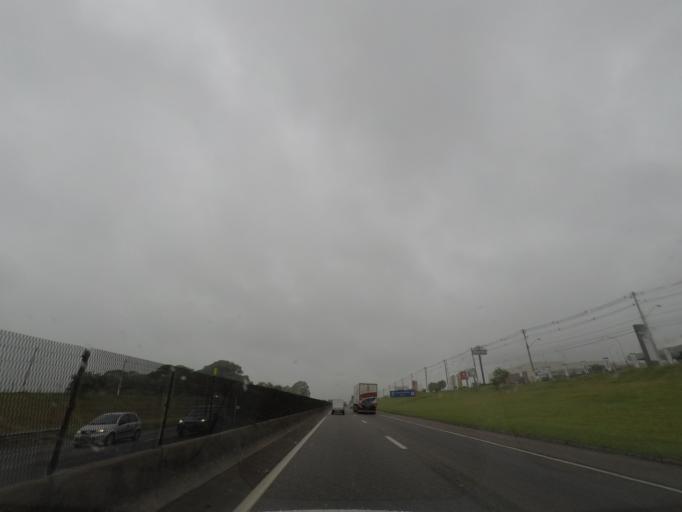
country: BR
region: Sao Paulo
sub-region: Taubate
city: Taubate
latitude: -23.0533
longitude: -45.6080
